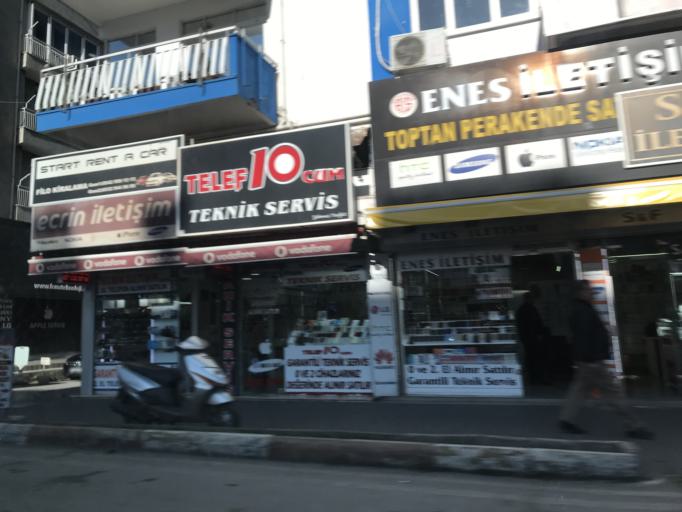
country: TR
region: Antalya
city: Antalya
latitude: 36.8926
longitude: 30.7011
